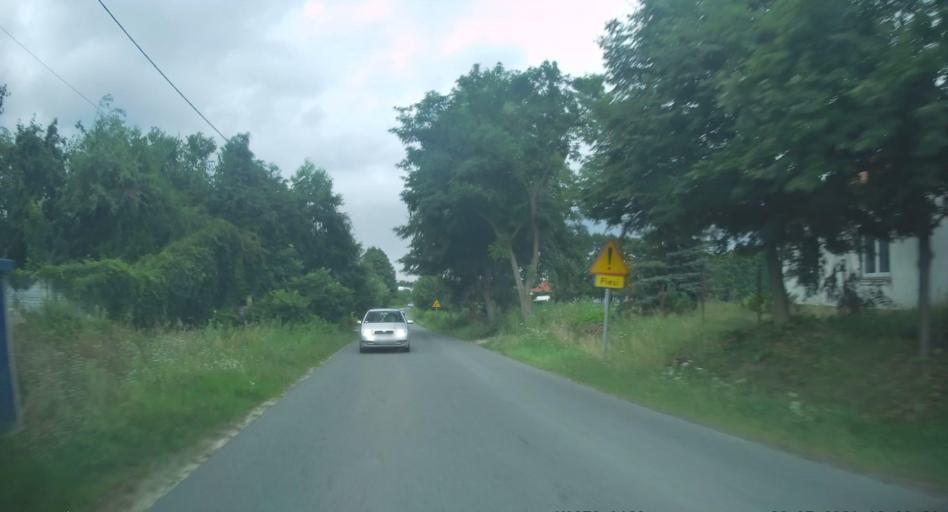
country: PL
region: Lodz Voivodeship
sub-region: Powiat rawski
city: Rawa Mazowiecka
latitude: 51.7491
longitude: 20.2134
